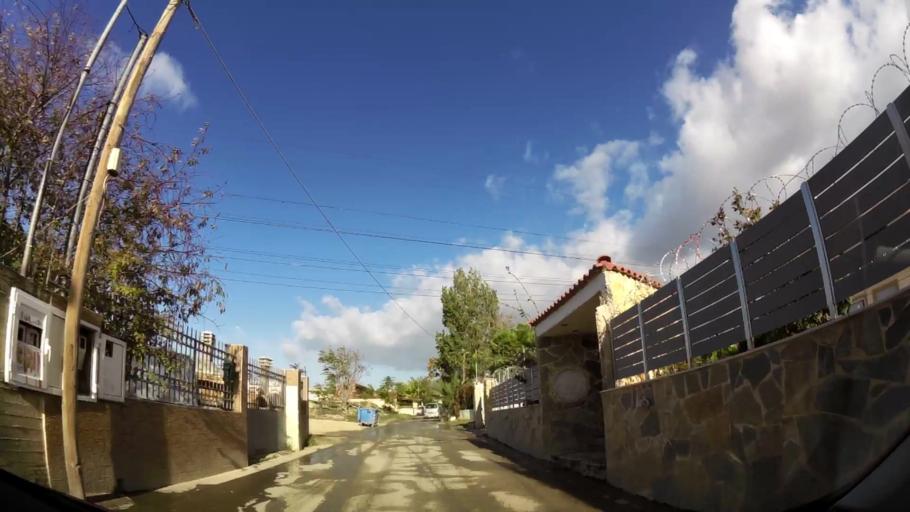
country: GR
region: Attica
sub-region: Nomarchia Athinas
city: Metamorfosi
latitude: 38.0752
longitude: 23.7490
